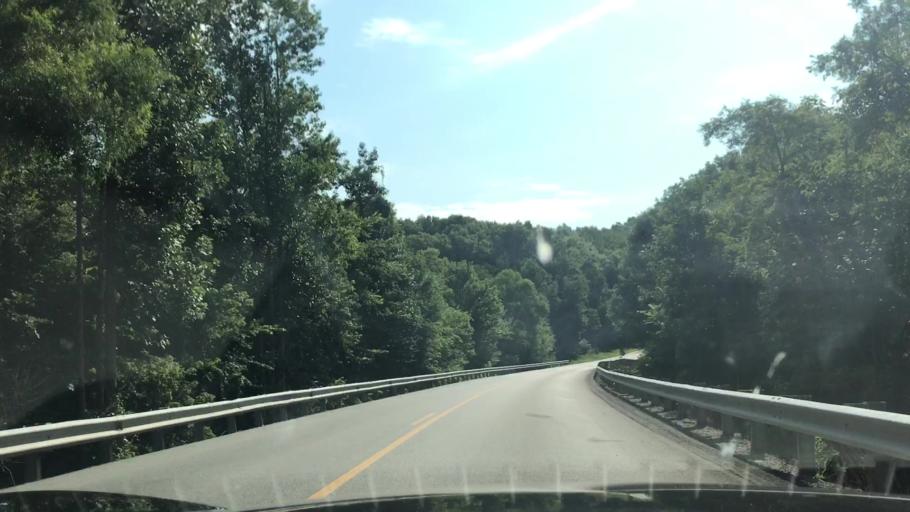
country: US
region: Kentucky
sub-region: Green County
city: Greensburg
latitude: 37.2271
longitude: -85.6746
